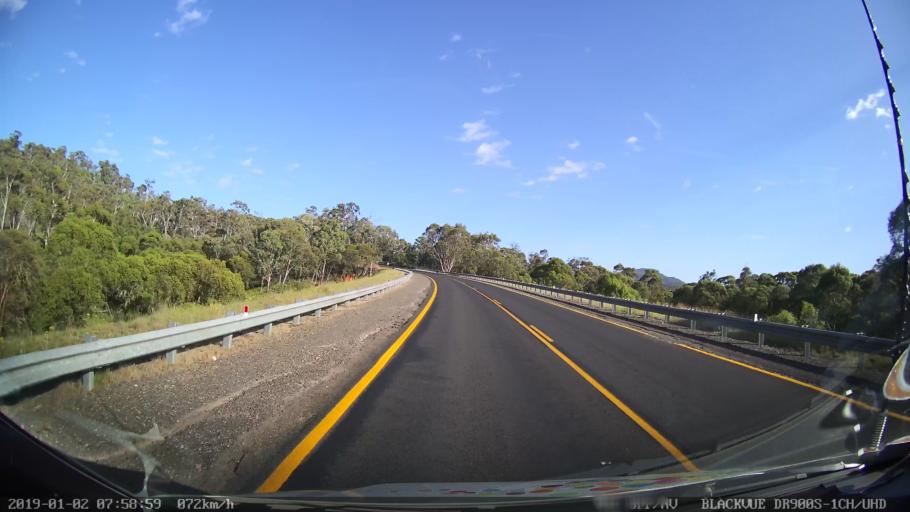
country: AU
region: New South Wales
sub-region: Tumut Shire
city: Tumut
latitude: -35.6485
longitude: 148.4622
